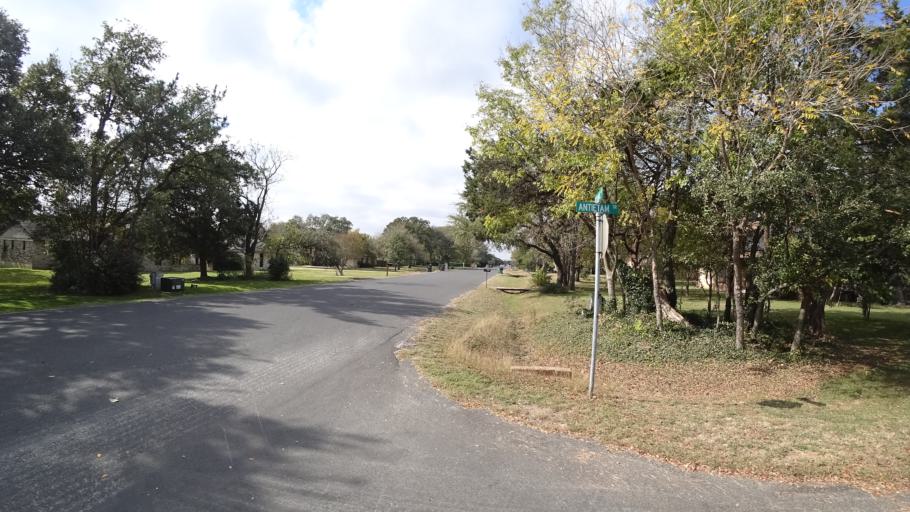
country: US
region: Texas
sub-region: Travis County
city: Shady Hollow
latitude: 30.1617
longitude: -97.8576
